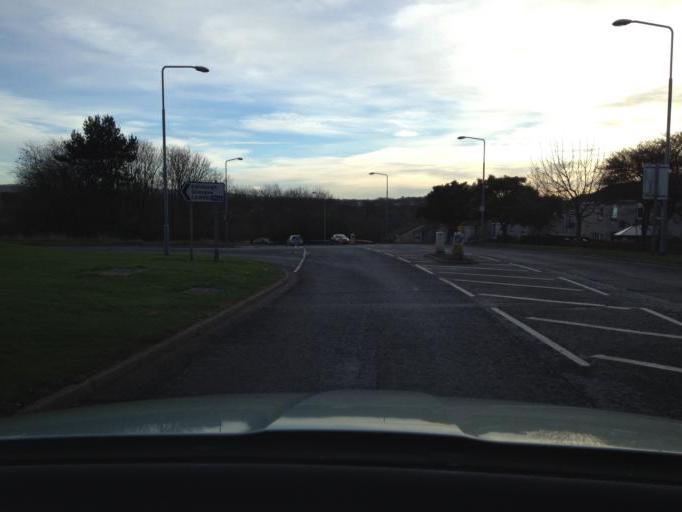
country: GB
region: Scotland
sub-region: West Lothian
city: Livingston
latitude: 55.8915
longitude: -3.5048
